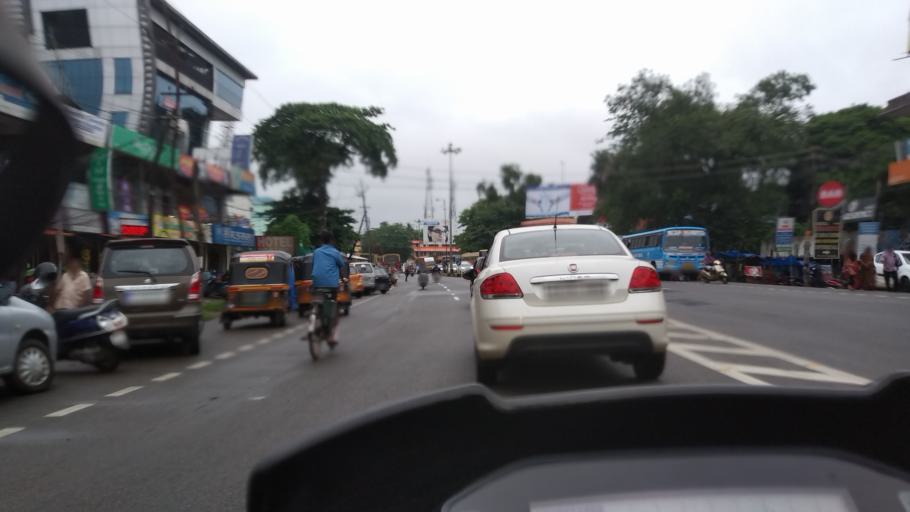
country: IN
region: Kerala
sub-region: Alappuzha
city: Mavelikara
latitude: 9.2786
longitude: 76.4596
